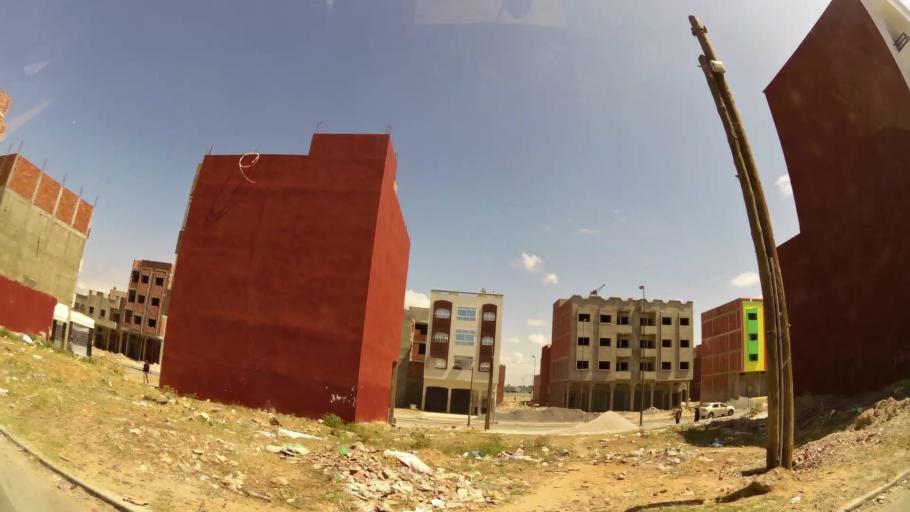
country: MA
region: Gharb-Chrarda-Beni Hssen
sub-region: Kenitra Province
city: Kenitra
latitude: 34.2397
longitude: -6.5443
